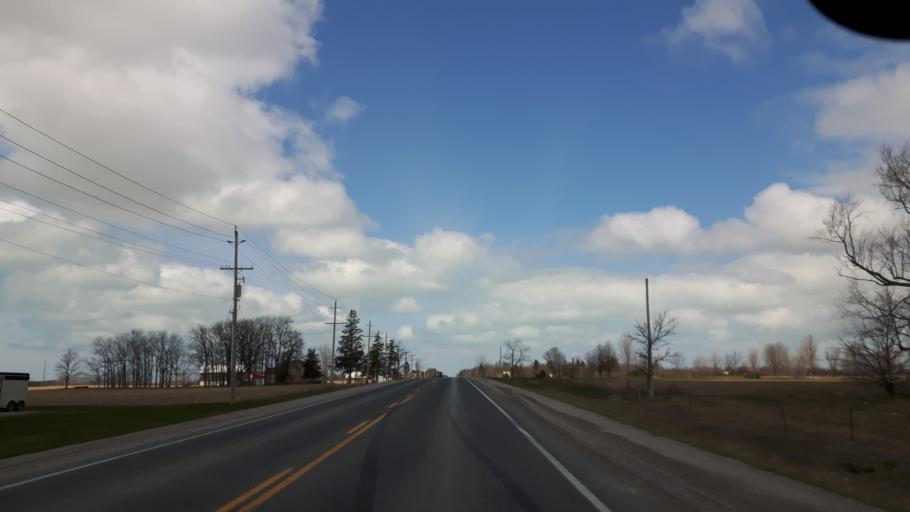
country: CA
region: Ontario
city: Goderich
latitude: 43.7186
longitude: -81.6723
